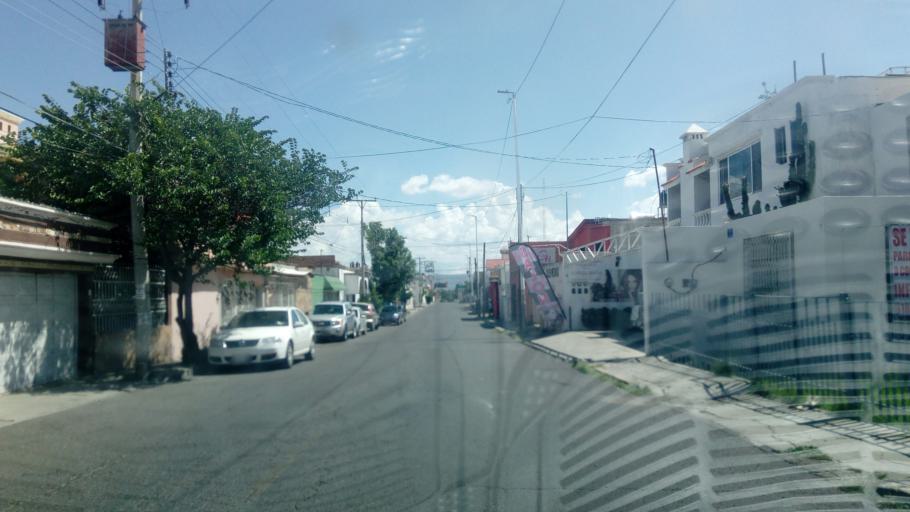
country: MX
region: Durango
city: Victoria de Durango
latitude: 24.0158
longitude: -104.6744
